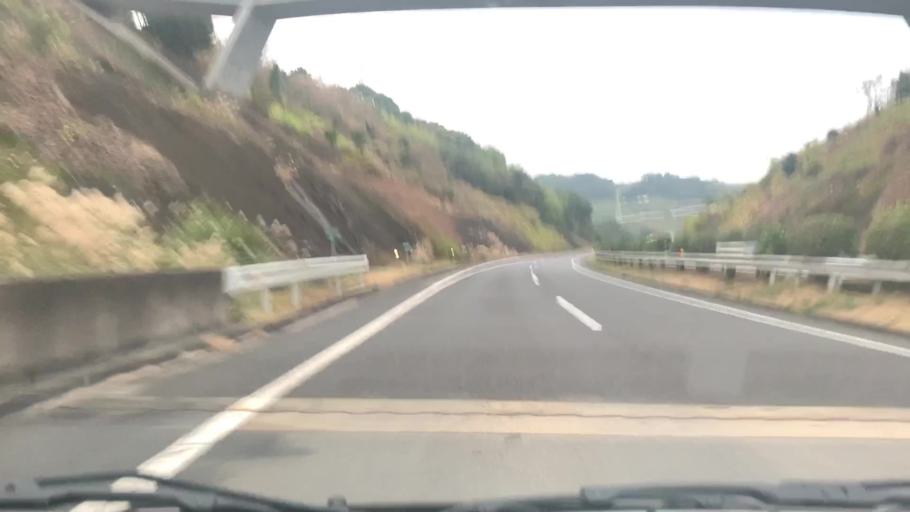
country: JP
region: Nagasaki
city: Omura
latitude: 33.0070
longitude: 129.9539
